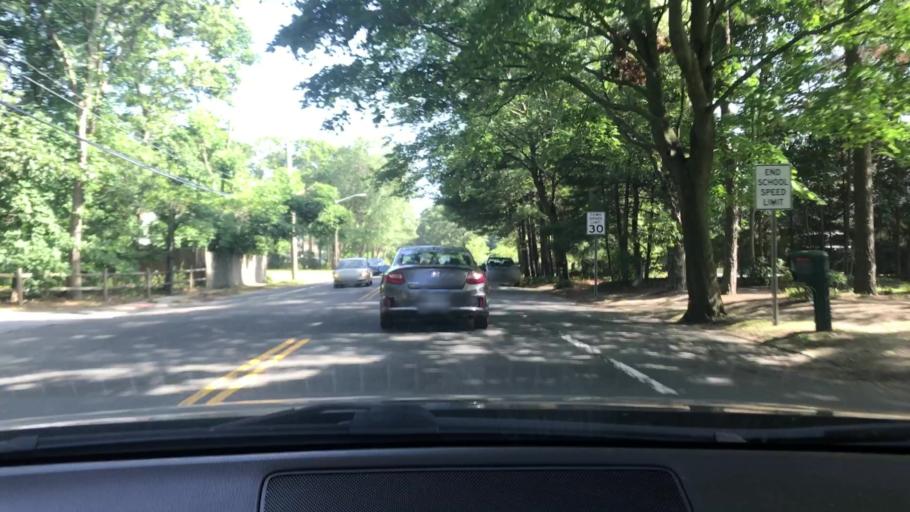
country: US
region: New York
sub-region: Suffolk County
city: Holbrook
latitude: 40.8214
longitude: -73.0800
